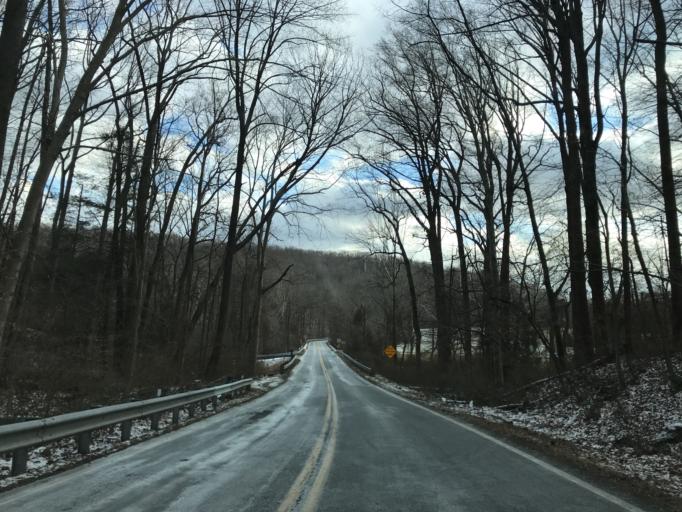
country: US
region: Maryland
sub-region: Harford County
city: Bel Air North
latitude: 39.6306
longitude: -76.3761
